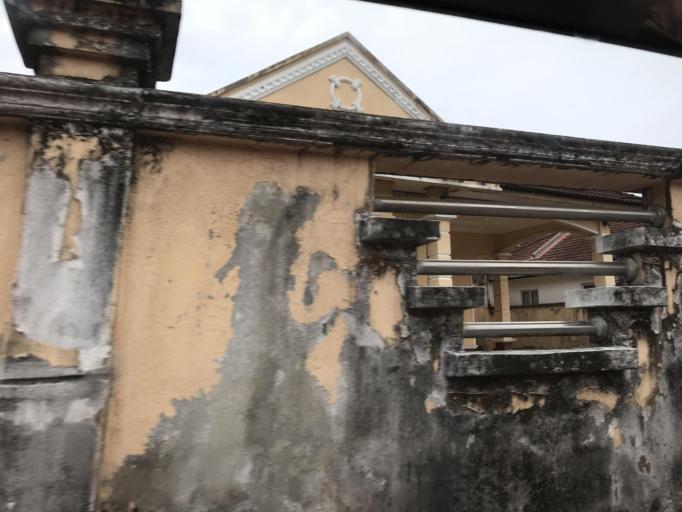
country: MY
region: Kelantan
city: Kota Bharu
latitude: 6.1167
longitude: 102.2082
